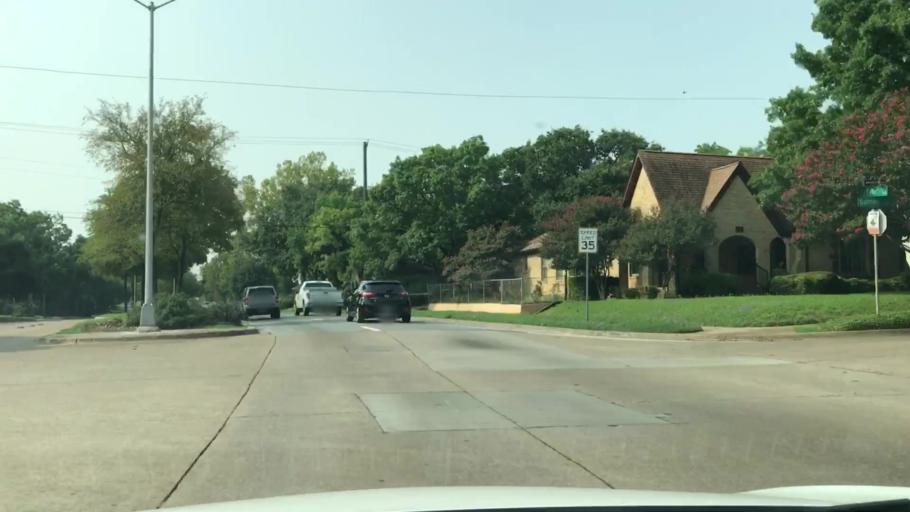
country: US
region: Texas
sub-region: Dallas County
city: Dallas
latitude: 32.7572
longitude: -96.8376
